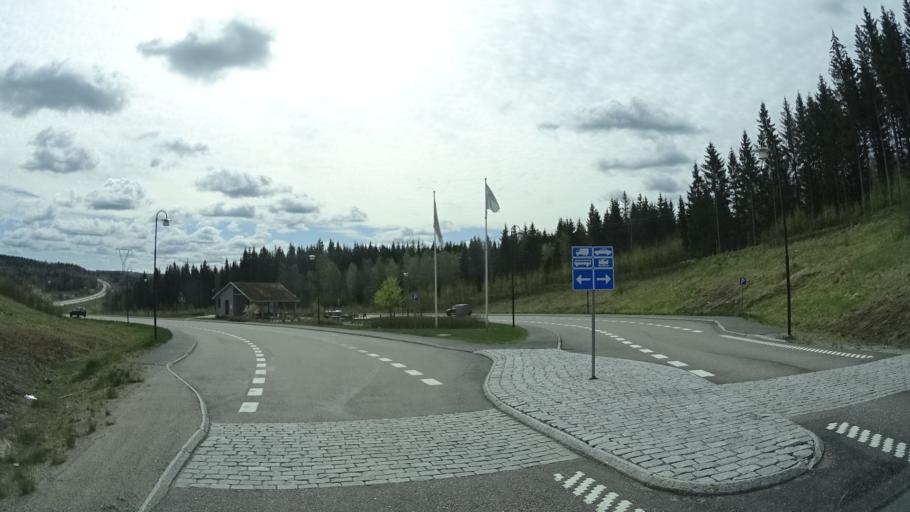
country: SE
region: Vaestra Goetaland
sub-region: Ulricehamns Kommun
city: Ulricehamn
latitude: 57.8178
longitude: 13.3419
